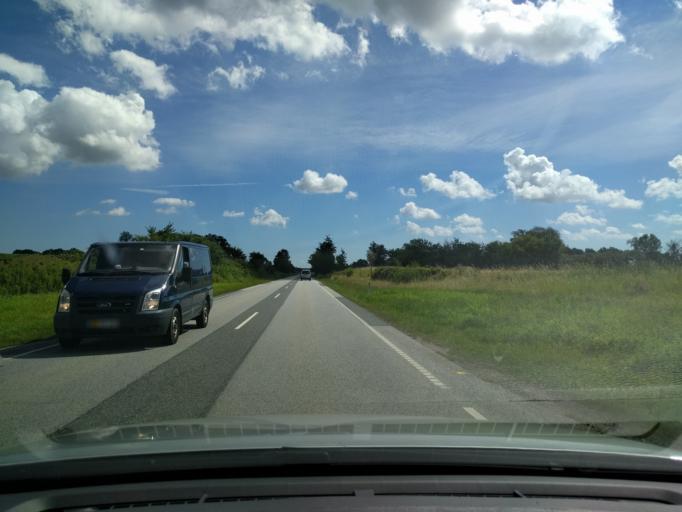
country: DK
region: Zealand
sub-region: Guldborgsund Kommune
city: Stubbekobing
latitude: 54.9266
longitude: 12.0191
